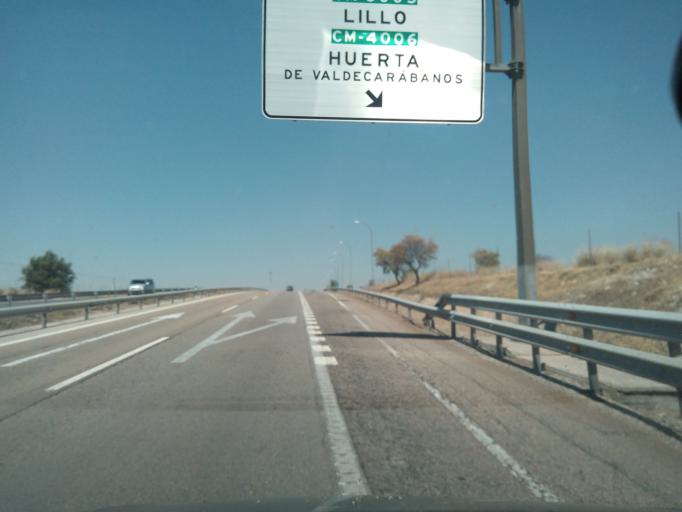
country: ES
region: Castille-La Mancha
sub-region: Province of Toledo
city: Tembleque
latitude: 39.7625
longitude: -3.4811
